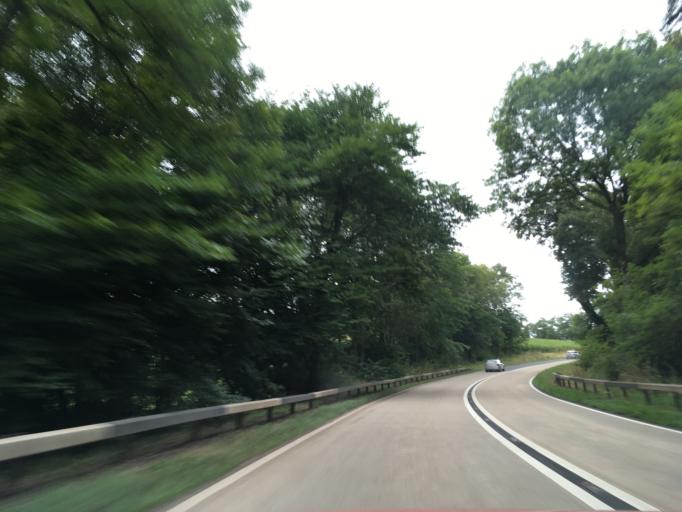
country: GB
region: Wales
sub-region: Sir Powys
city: Brecon
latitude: 51.9453
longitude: -3.4967
